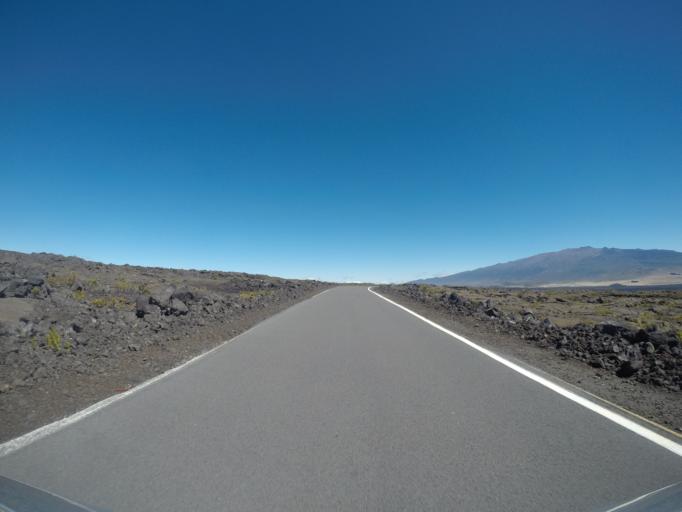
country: US
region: Hawaii
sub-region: Hawaii County
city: Volcano
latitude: 19.6210
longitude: -155.4737
